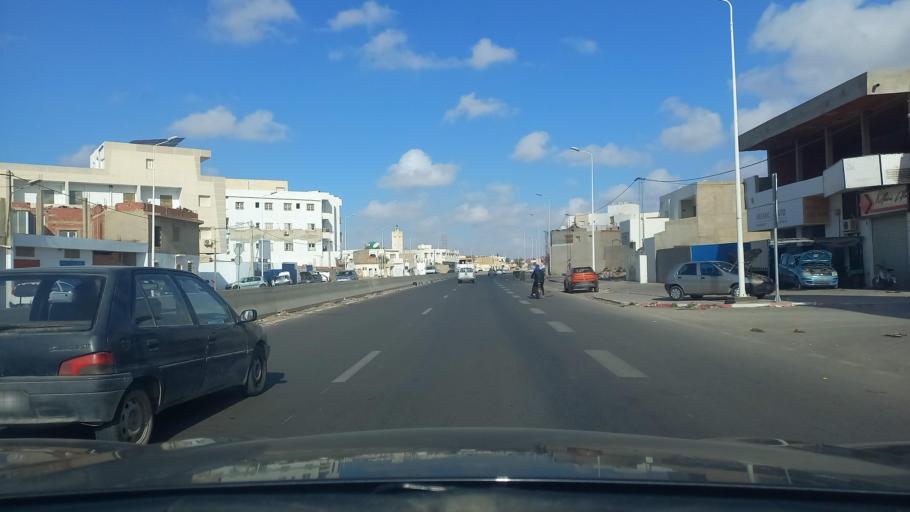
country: TN
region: Safaqis
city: Sfax
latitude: 34.7382
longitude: 10.7238
